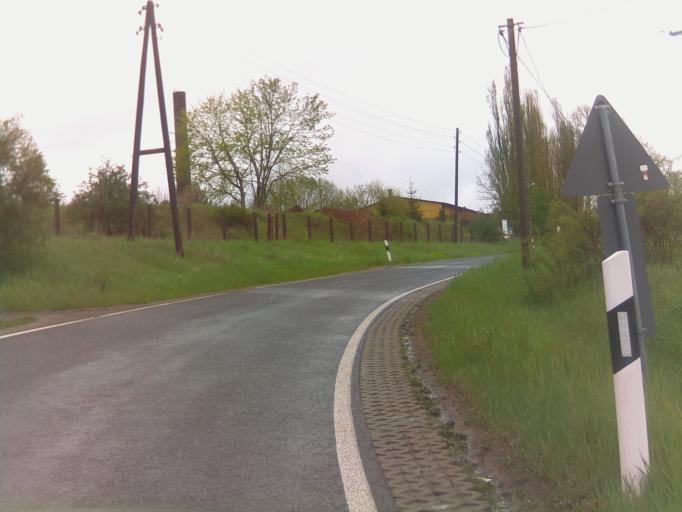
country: DE
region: Thuringia
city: Kloster Vessra
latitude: 50.4954
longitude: 10.6470
